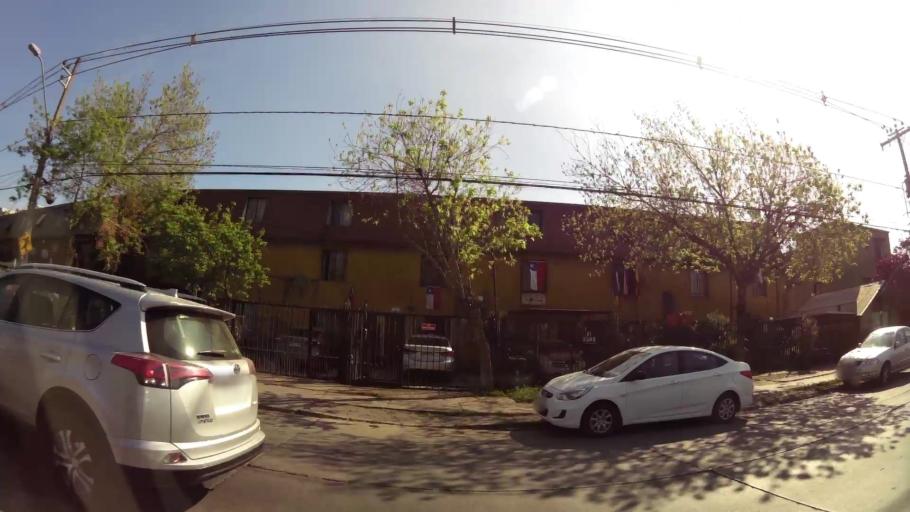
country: CL
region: Santiago Metropolitan
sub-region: Provincia de Santiago
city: Santiago
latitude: -33.4682
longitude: -70.6232
